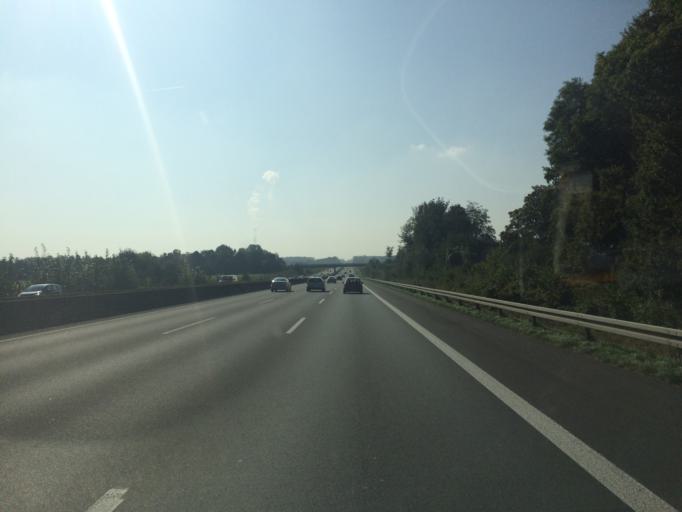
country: DE
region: North Rhine-Westphalia
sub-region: Regierungsbezirk Munster
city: Beckum
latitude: 51.7641
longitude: 8.0039
